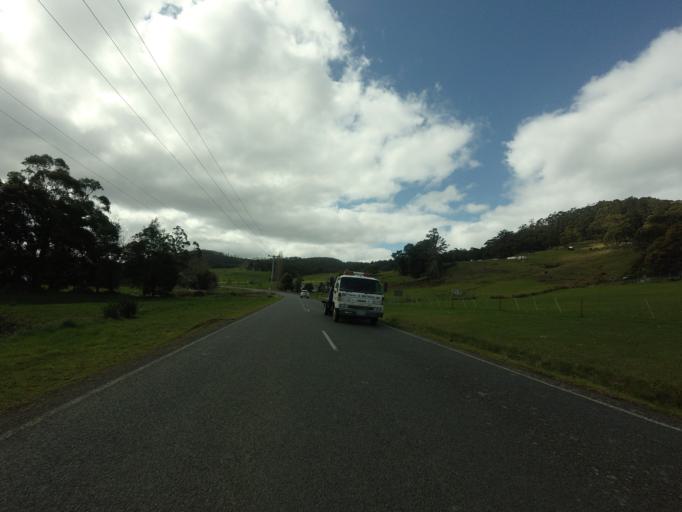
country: AU
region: Tasmania
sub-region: Huon Valley
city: Cygnet
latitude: -43.2968
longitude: 147.0108
